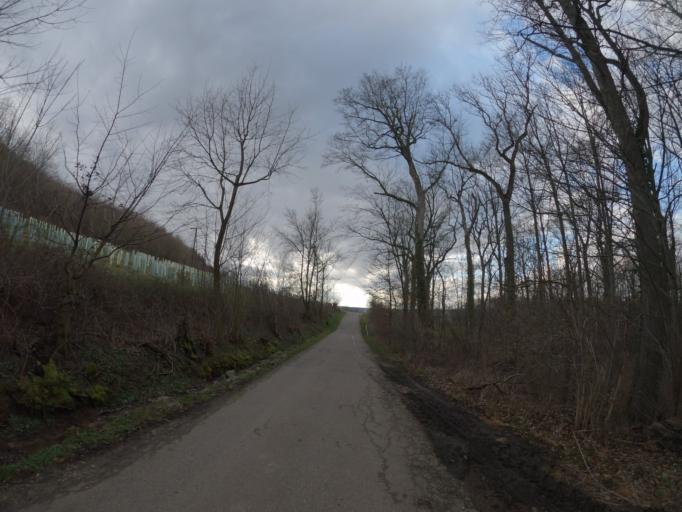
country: DE
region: Baden-Wuerttemberg
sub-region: Regierungsbezirk Stuttgart
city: Eschenbach
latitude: 48.6554
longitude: 9.6854
